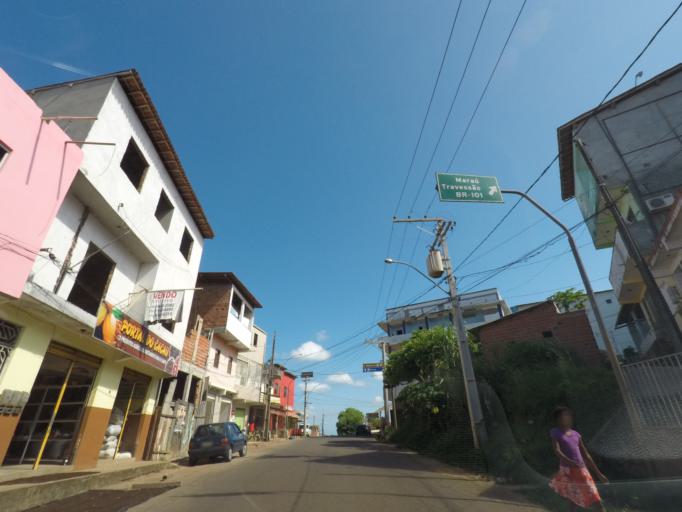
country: BR
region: Bahia
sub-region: Camamu
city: Camamu
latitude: -13.9411
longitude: -39.1039
